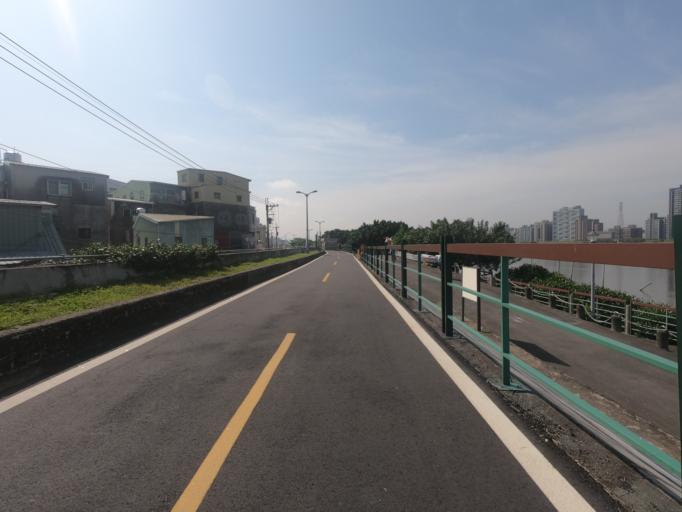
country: TW
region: Taipei
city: Taipei
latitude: 25.0961
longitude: 121.4939
